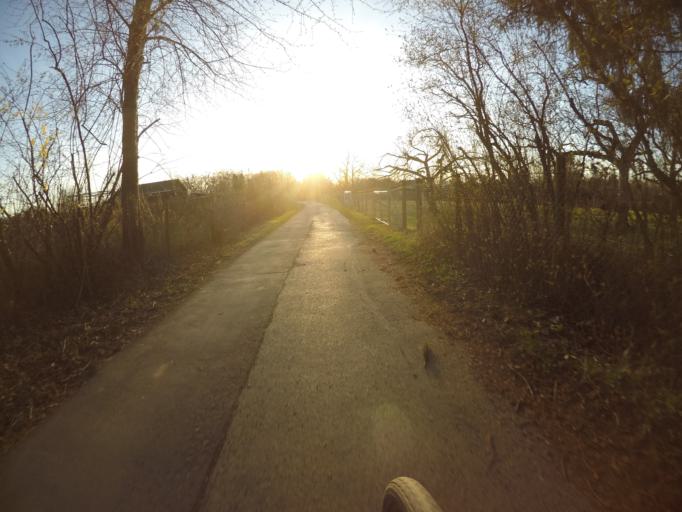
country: DE
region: Baden-Wuerttemberg
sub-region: Regierungsbezirk Stuttgart
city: Leinfelden-Echterdingen
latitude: 48.7377
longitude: 9.1391
